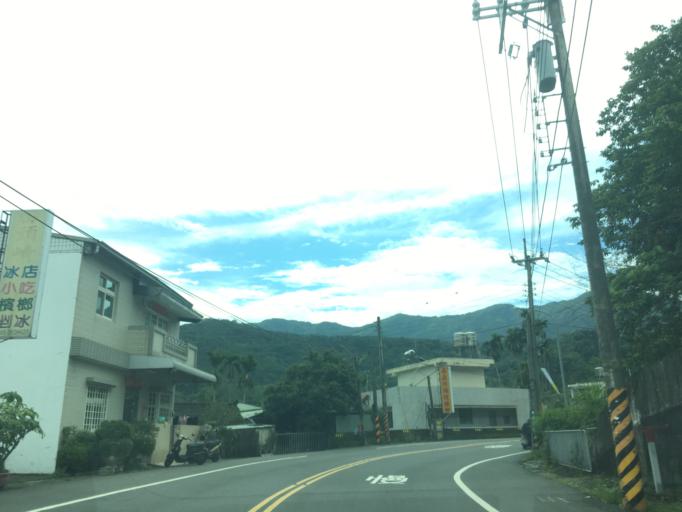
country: TW
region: Taiwan
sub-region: Yunlin
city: Douliu
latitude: 23.5819
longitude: 120.5643
